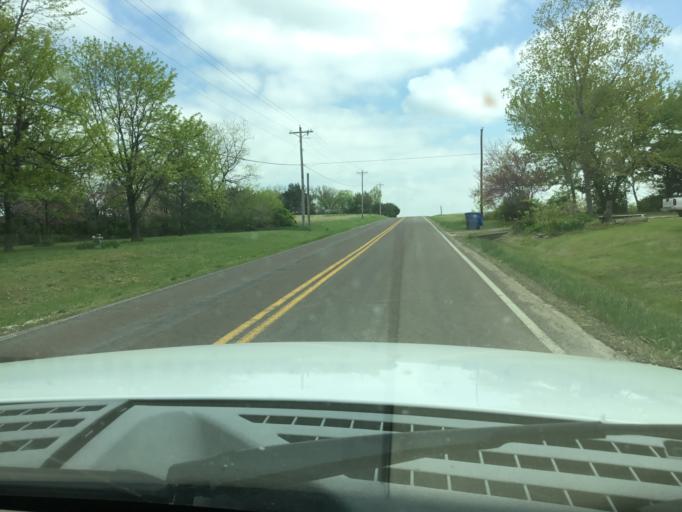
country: US
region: Kansas
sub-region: Shawnee County
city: Auburn
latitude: 38.9562
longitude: -95.8085
